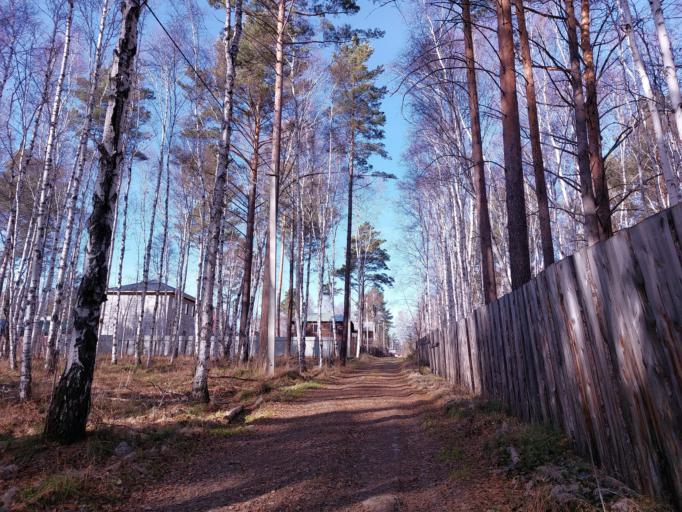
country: RU
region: Irkutsk
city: Pivovarikha
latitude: 52.1853
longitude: 104.4562
